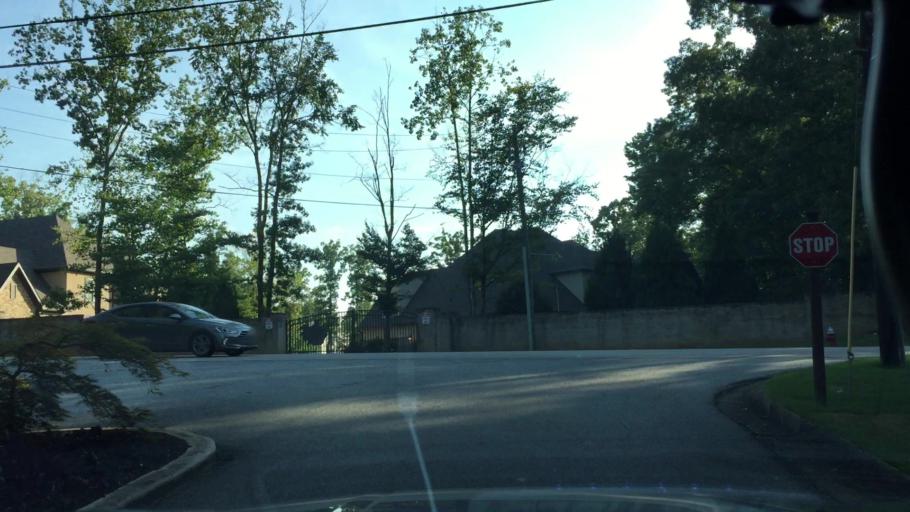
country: US
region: Alabama
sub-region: Lee County
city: Opelika
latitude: 32.5982
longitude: -85.4178
